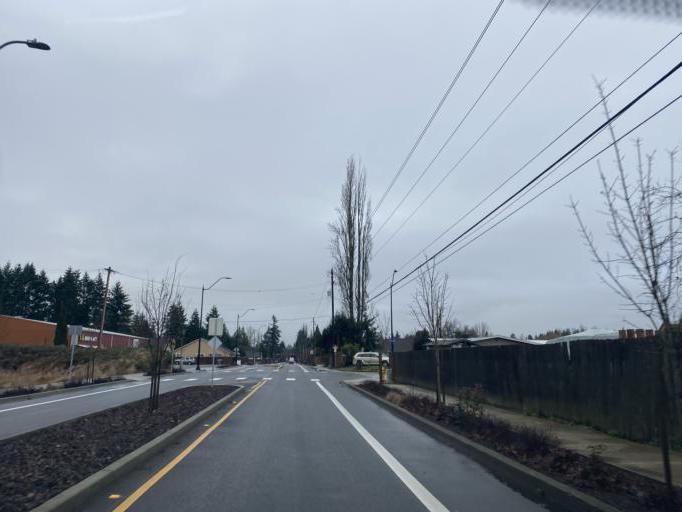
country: US
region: Washington
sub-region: Clark County
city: Battle Ground
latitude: 45.7705
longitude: -122.5373
